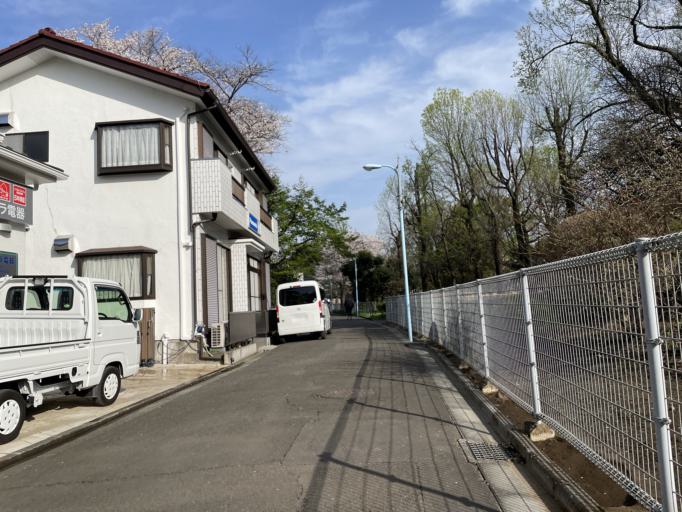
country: JP
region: Tokyo
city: Tokyo
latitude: 35.6867
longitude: 139.6352
